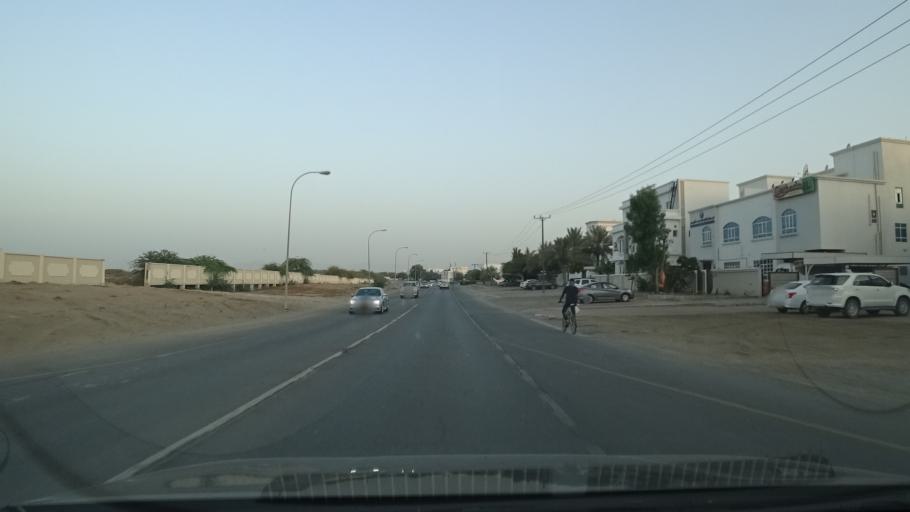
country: OM
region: Muhafazat Masqat
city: As Sib al Jadidah
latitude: 23.6379
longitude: 58.2416
